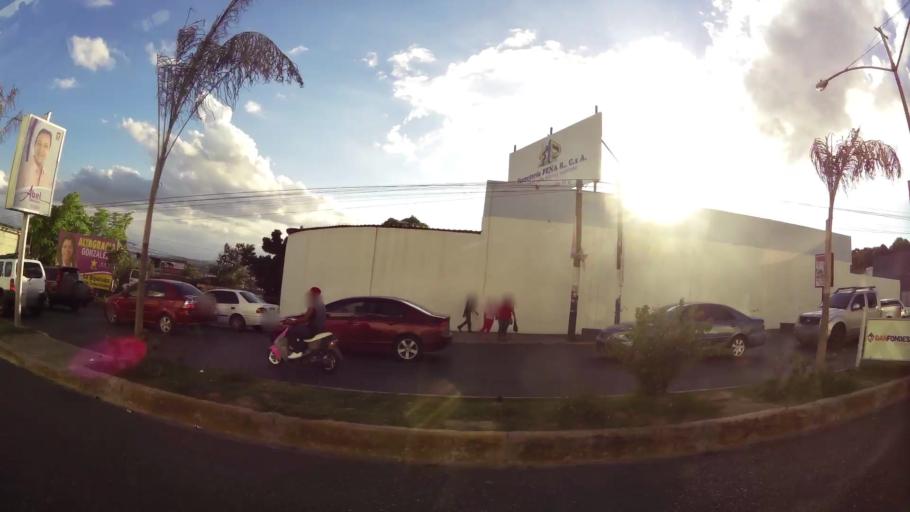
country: DO
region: Santiago
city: Santiago de los Caballeros
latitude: 19.4730
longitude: -70.7142
